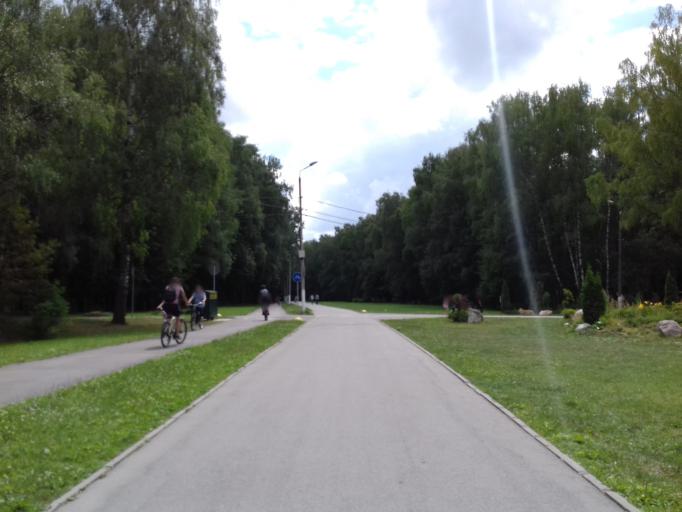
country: RU
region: Tula
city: Tula
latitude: 54.1829
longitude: 37.5827
